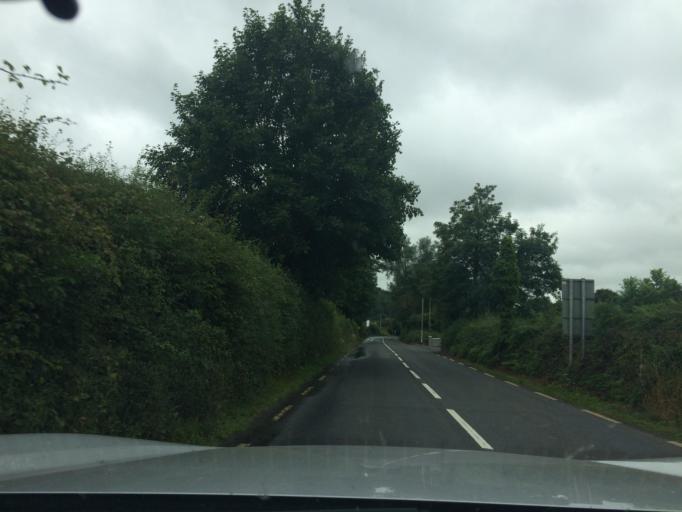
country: IE
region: Munster
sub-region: South Tipperary
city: Cluain Meala
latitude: 52.3387
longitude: -7.7267
